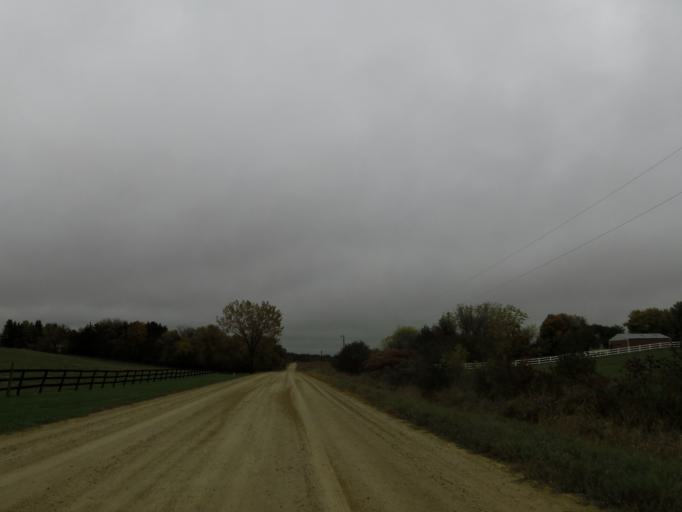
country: US
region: Minnesota
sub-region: Scott County
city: Prior Lake
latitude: 44.6853
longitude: -93.4322
